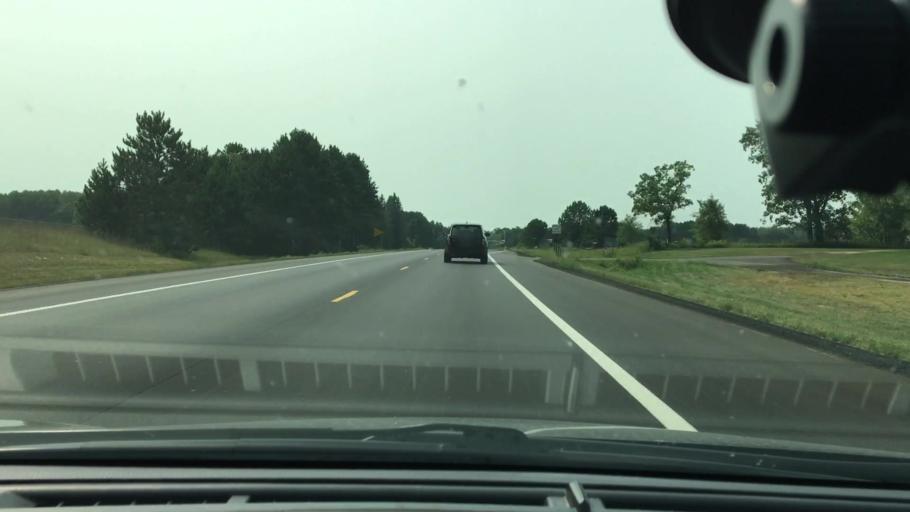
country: US
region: Minnesota
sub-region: Crow Wing County
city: Brainerd
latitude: 46.4039
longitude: -94.1761
